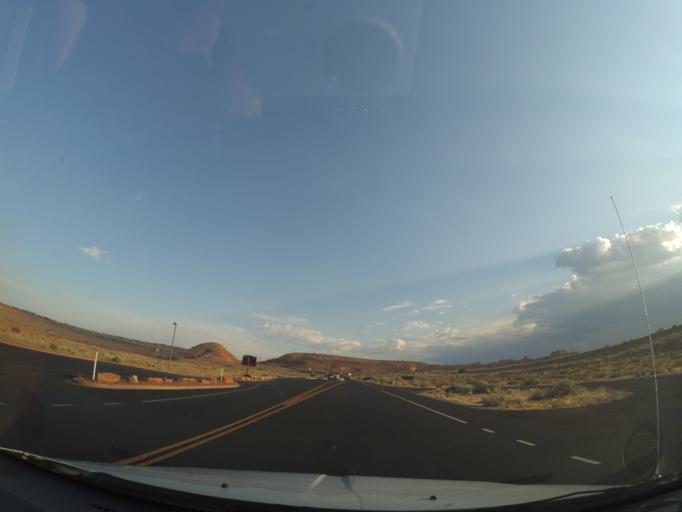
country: US
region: Arizona
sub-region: Coconino County
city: Page
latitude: 36.9442
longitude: -111.4936
